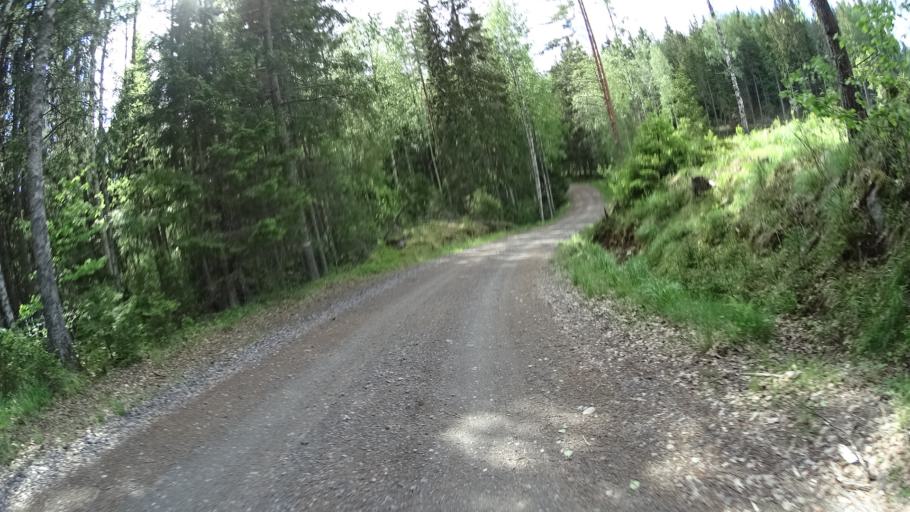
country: FI
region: Varsinais-Suomi
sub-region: Salo
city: Kisko
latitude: 60.1803
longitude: 23.5376
